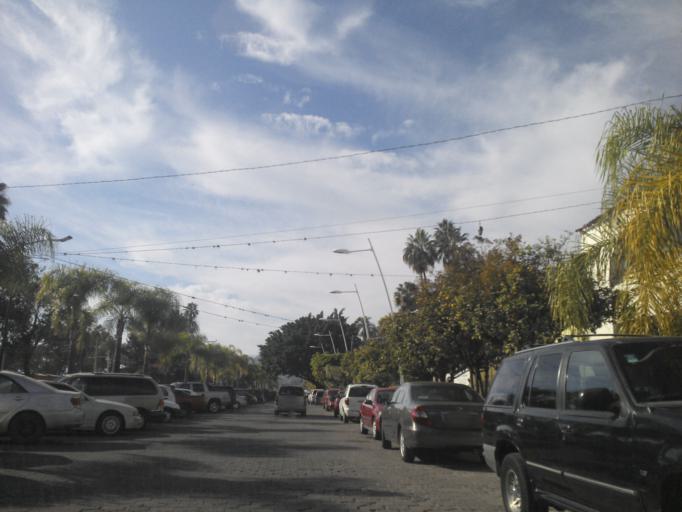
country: MX
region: Jalisco
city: Chapala
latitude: 20.2874
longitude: -103.1908
